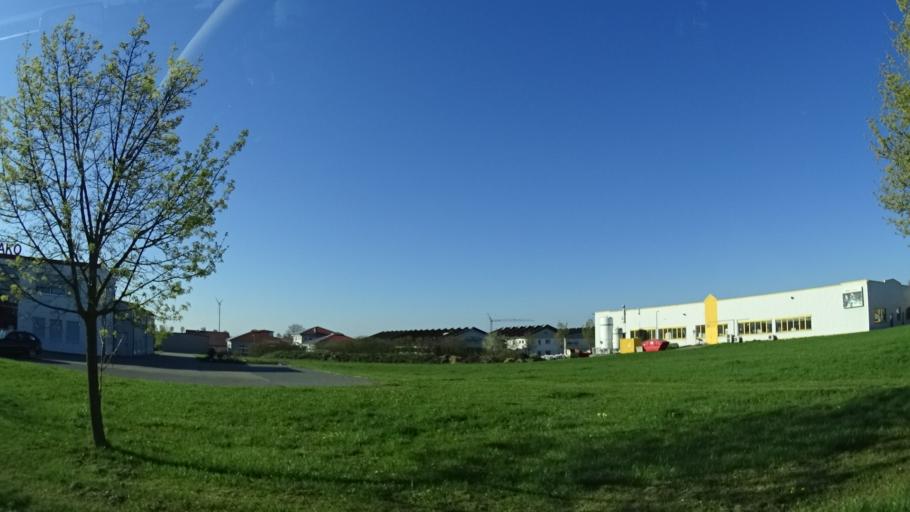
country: DE
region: Baden-Wuerttemberg
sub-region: Regierungsbezirk Stuttgart
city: Wolpertshausen
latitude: 49.1692
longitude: 9.8530
